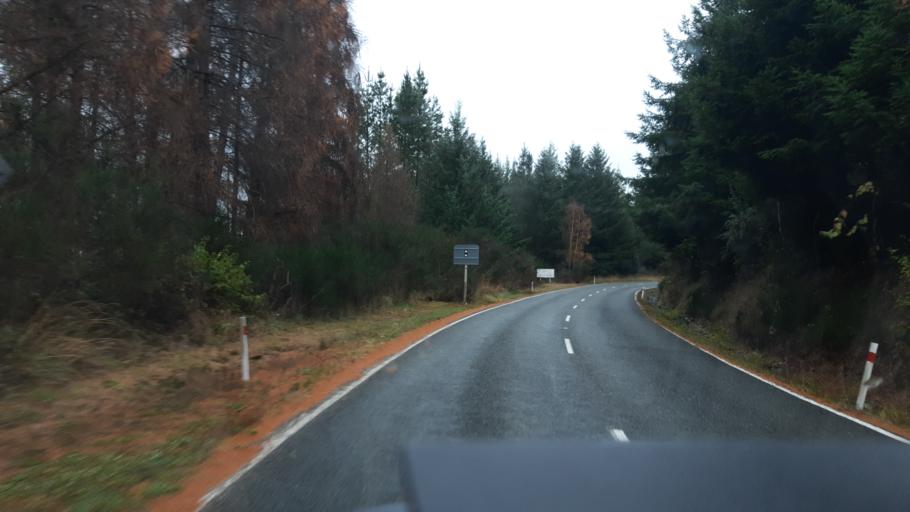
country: NZ
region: Tasman
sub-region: Tasman District
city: Wakefield
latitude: -41.6669
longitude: 172.8742
